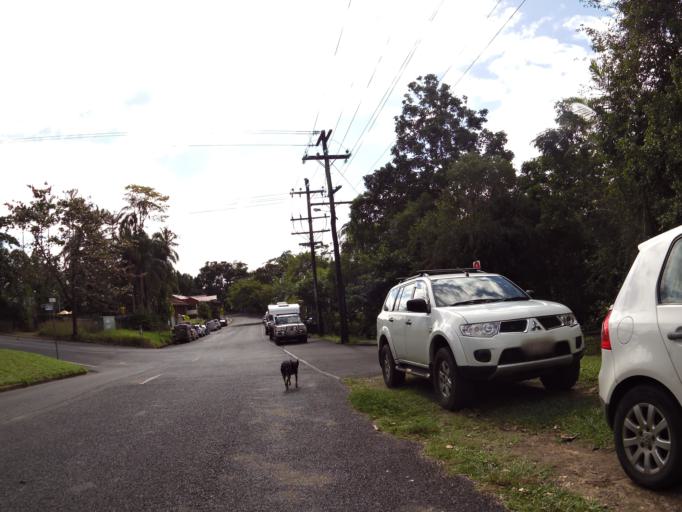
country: AU
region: Queensland
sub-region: Tablelands
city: Kuranda
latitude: -16.8194
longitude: 145.6386
